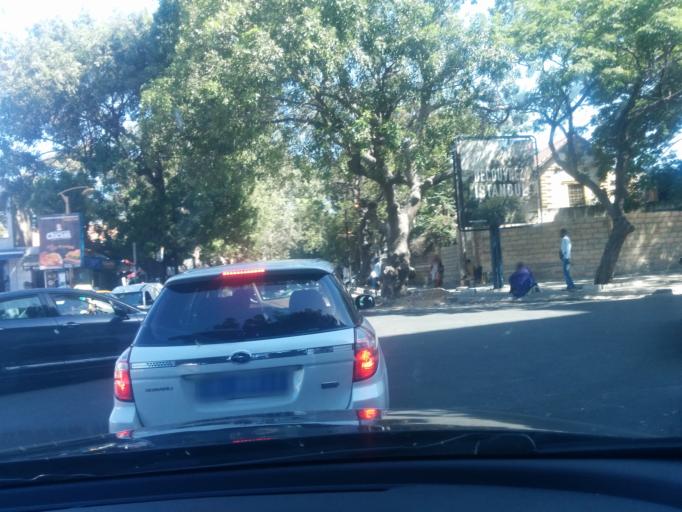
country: SN
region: Dakar
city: Dakar
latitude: 14.6690
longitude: -17.4397
